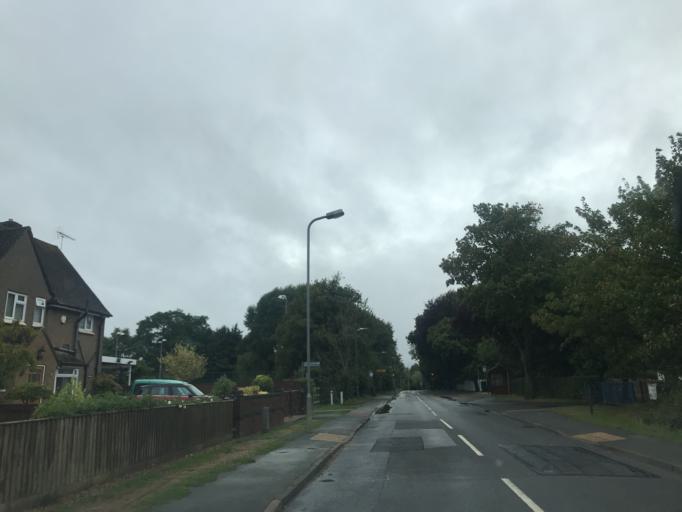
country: GB
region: England
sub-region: Buckinghamshire
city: Haddenham
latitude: 51.7731
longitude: -0.9213
